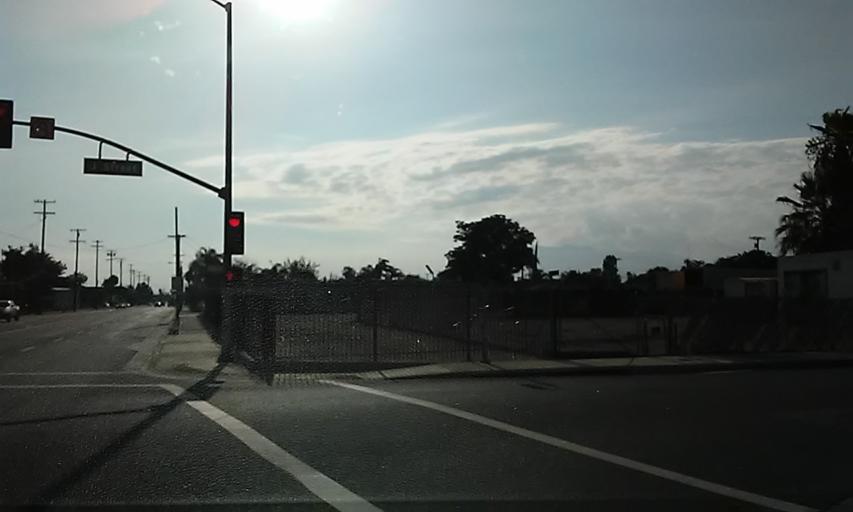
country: US
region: California
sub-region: San Bernardino County
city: San Bernardino
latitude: 34.1084
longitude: -117.3055
